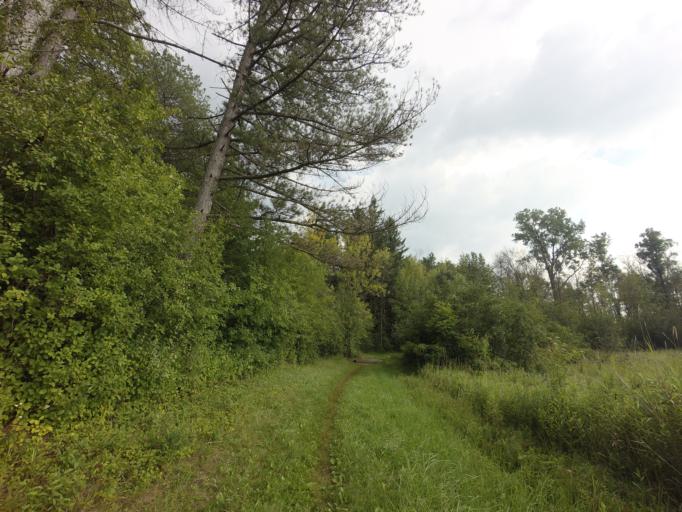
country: US
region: Wisconsin
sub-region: Washington County
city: Kewaskum
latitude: 43.5917
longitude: -88.1759
